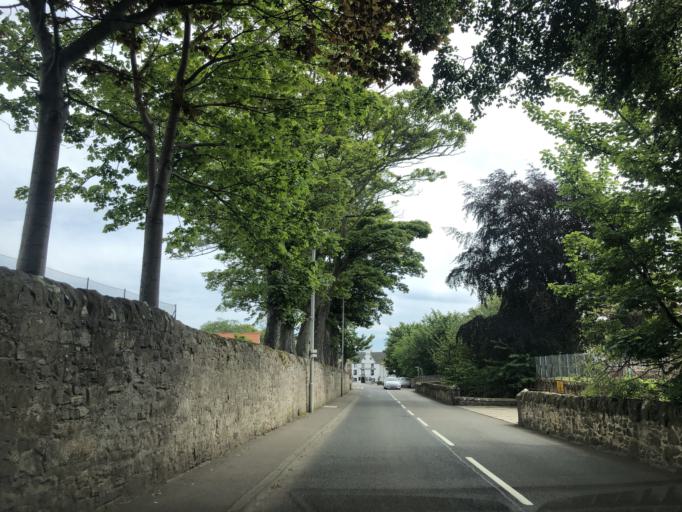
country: GB
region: Scotland
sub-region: Fife
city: Anstruther
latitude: 56.2616
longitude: -2.6292
